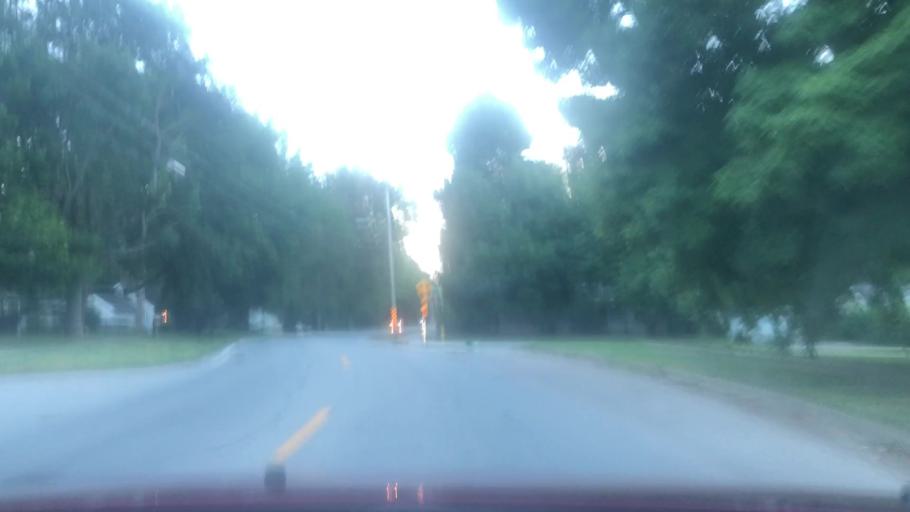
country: US
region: Missouri
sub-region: Greene County
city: Springfield
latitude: 37.1798
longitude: -93.2470
